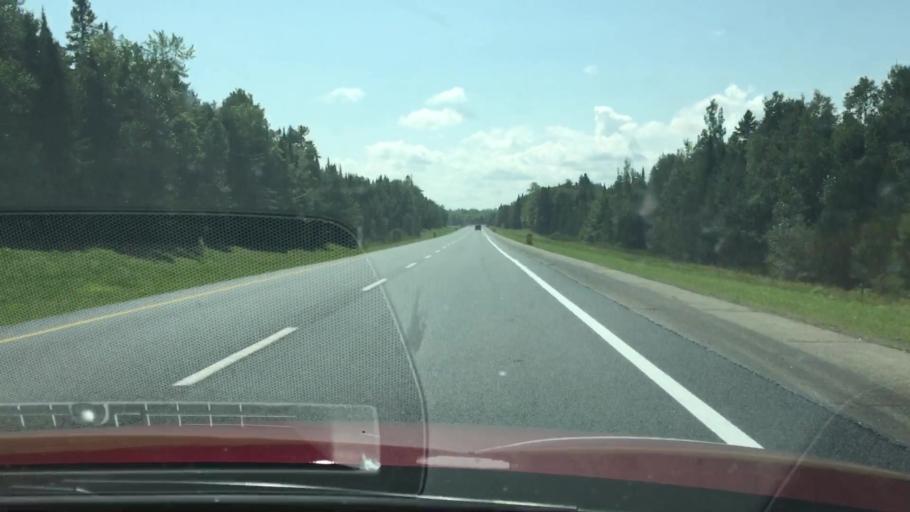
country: US
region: Maine
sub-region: Penobscot County
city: Patten
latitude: 45.8501
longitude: -68.4284
